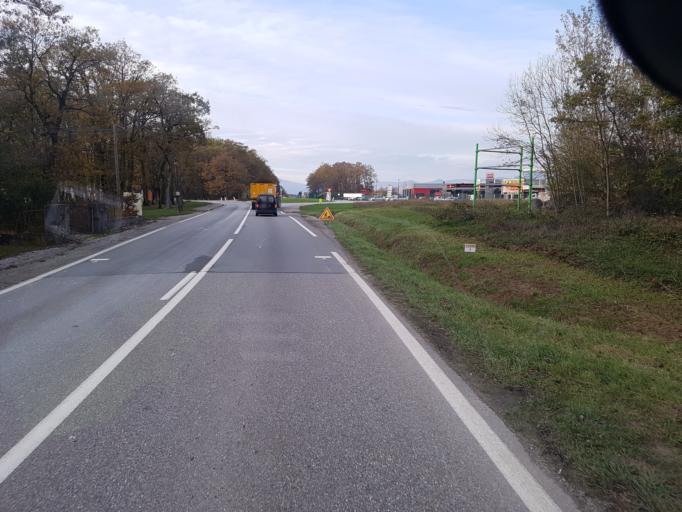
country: FR
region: Rhone-Alpes
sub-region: Departement de l'Ain
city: Bellegarde-sur-Valserine
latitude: 46.0605
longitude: 5.8661
